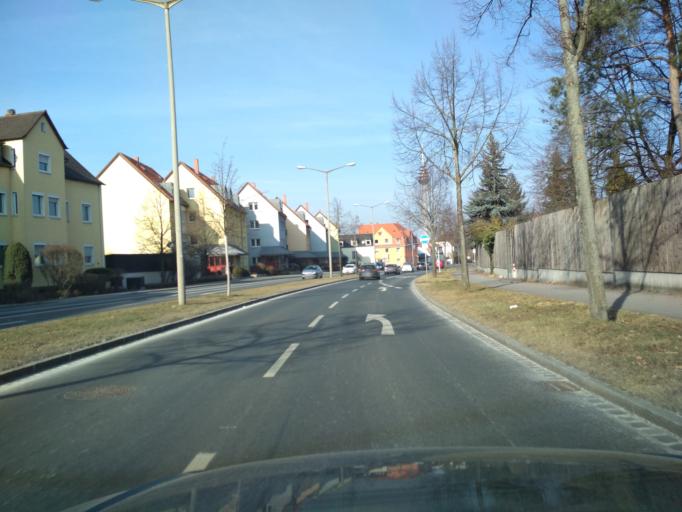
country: DE
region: Bavaria
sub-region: Regierungsbezirk Mittelfranken
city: Stein
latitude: 49.4121
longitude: 11.0340
